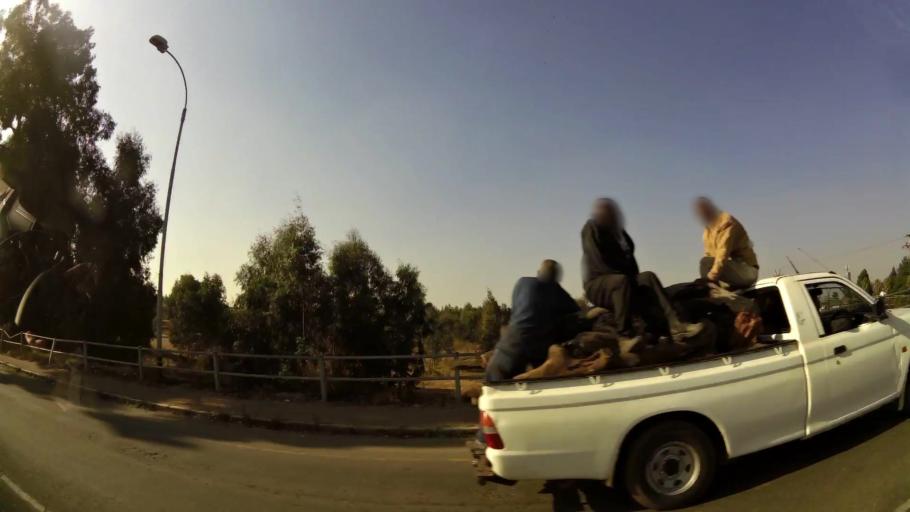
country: ZA
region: Gauteng
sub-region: West Rand District Municipality
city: Randfontein
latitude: -26.1560
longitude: 27.7174
